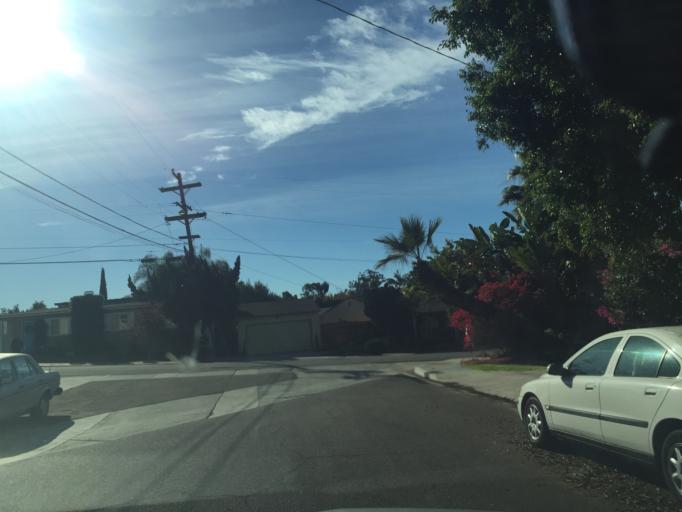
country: US
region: California
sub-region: San Diego County
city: Lemon Grove
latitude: 32.7636
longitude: -117.0818
